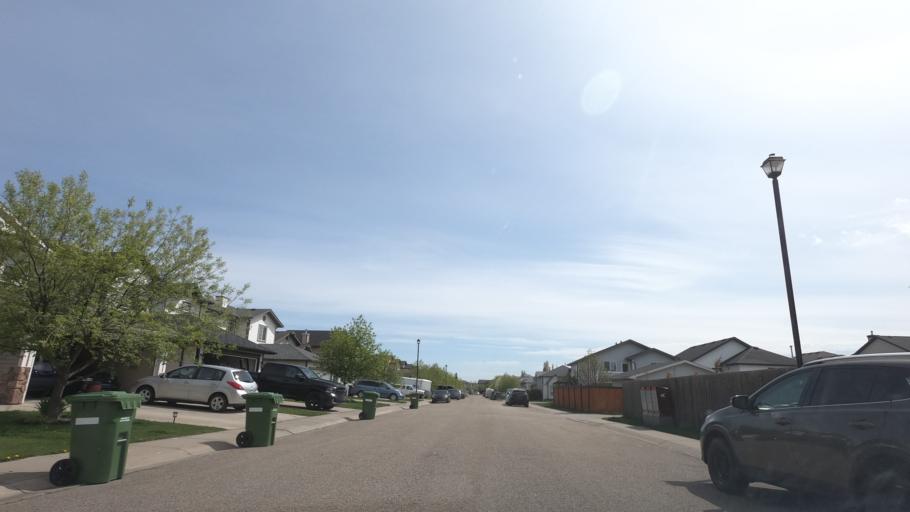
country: CA
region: Alberta
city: Airdrie
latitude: 51.3068
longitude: -114.0212
